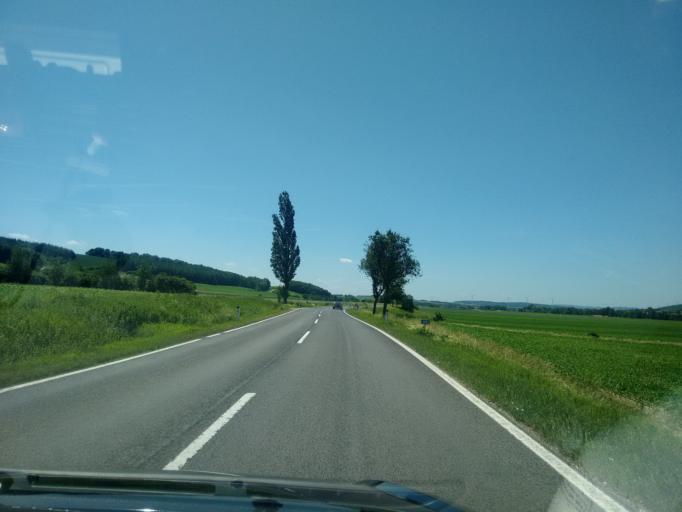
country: AT
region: Lower Austria
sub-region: Politischer Bezirk Tulln
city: Wurmla
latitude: 48.2723
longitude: 15.8400
